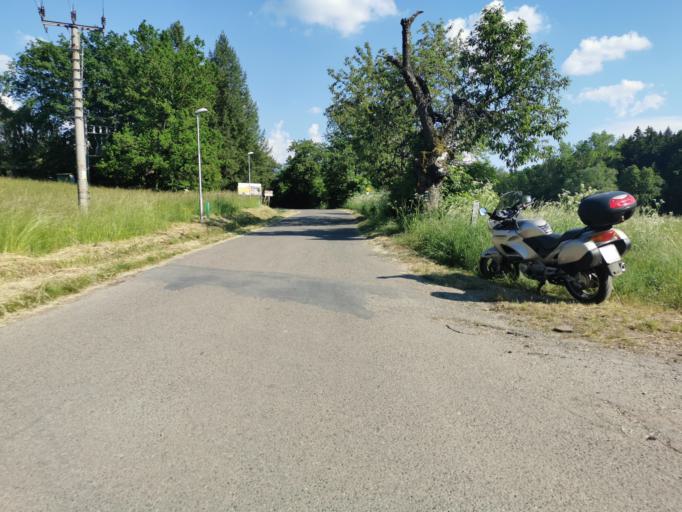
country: CZ
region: South Moravian
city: Knezdub
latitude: 48.8614
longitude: 17.3905
